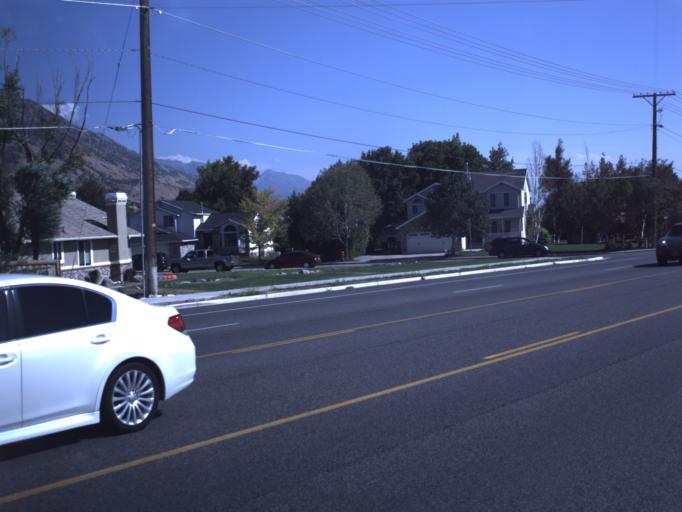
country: US
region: Utah
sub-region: Utah County
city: Cedar Hills
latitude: 40.4289
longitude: -111.7736
